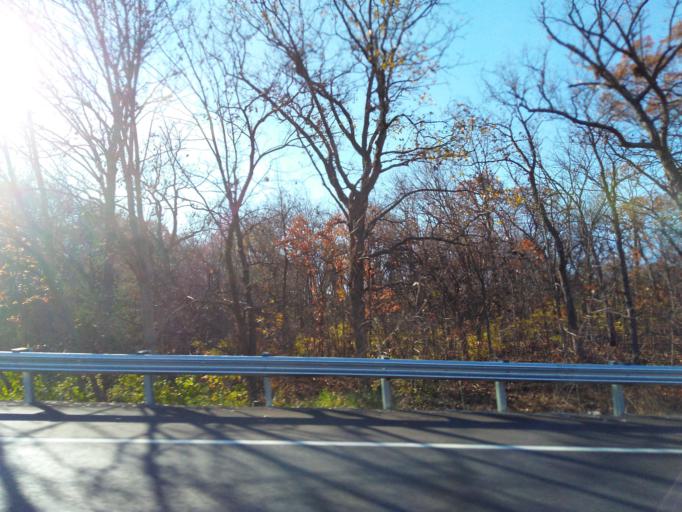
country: US
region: Illinois
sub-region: Madison County
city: Highland
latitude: 38.7861
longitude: -89.6999
